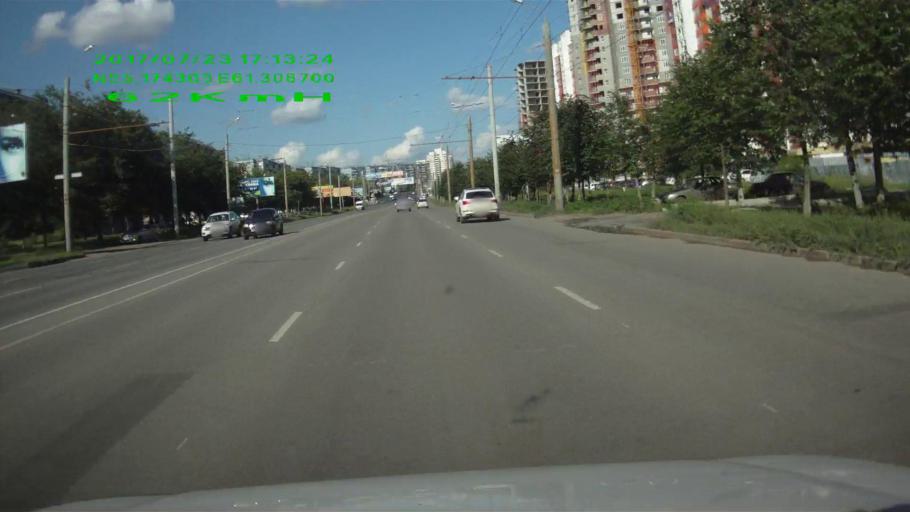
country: RU
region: Chelyabinsk
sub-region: Gorod Chelyabinsk
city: Chelyabinsk
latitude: 55.1745
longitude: 61.3072
